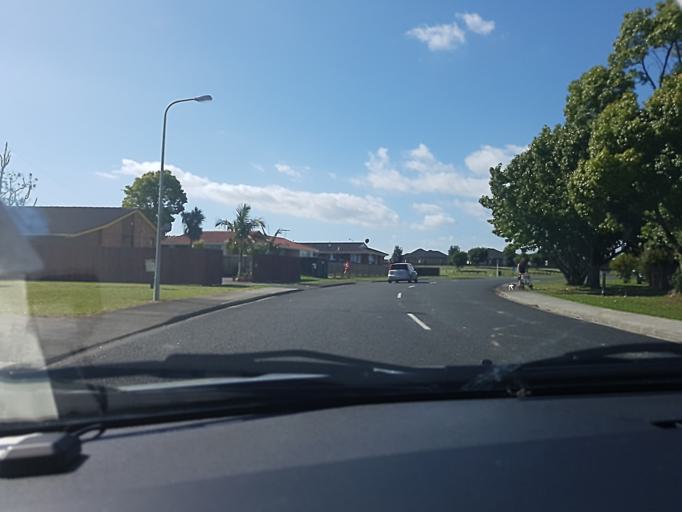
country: NZ
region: Auckland
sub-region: Auckland
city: Papakura
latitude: -37.0768
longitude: 174.9310
